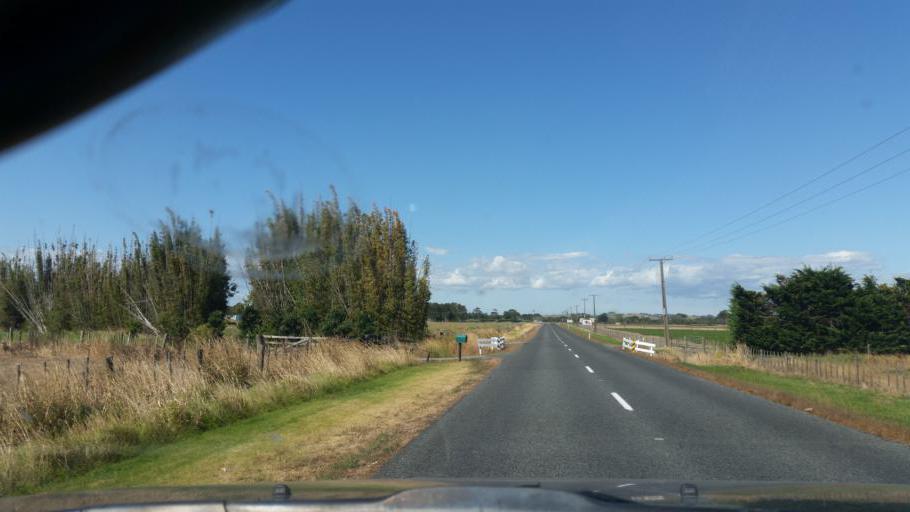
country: NZ
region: Northland
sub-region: Kaipara District
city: Dargaville
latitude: -35.9456
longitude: 173.8371
